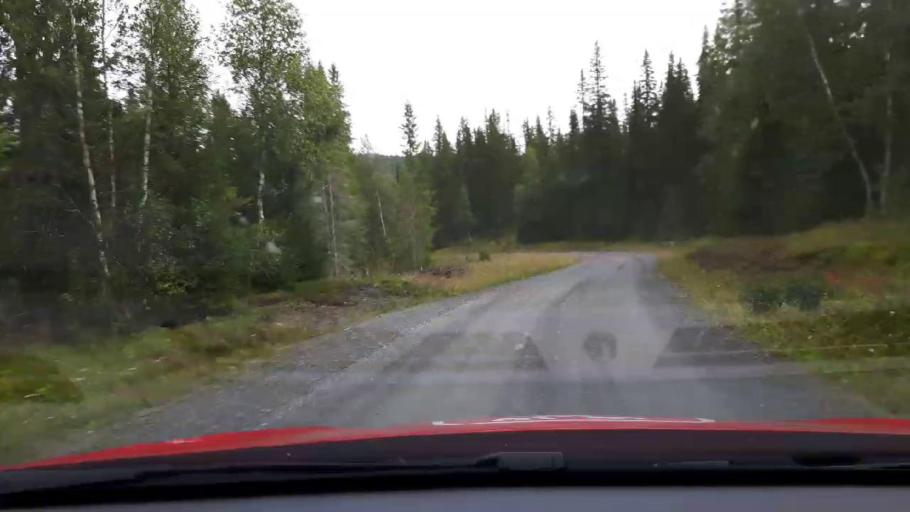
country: SE
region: Jaemtland
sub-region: Are Kommun
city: Are
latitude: 63.7732
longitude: 13.0745
